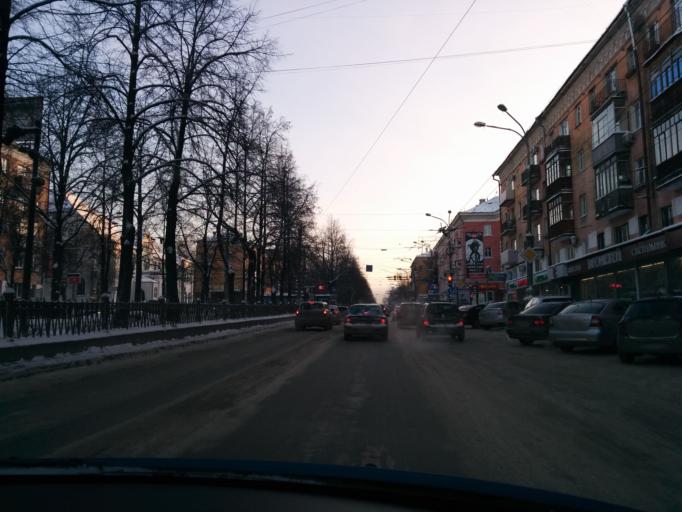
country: RU
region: Perm
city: Perm
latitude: 58.0071
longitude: 56.2427
